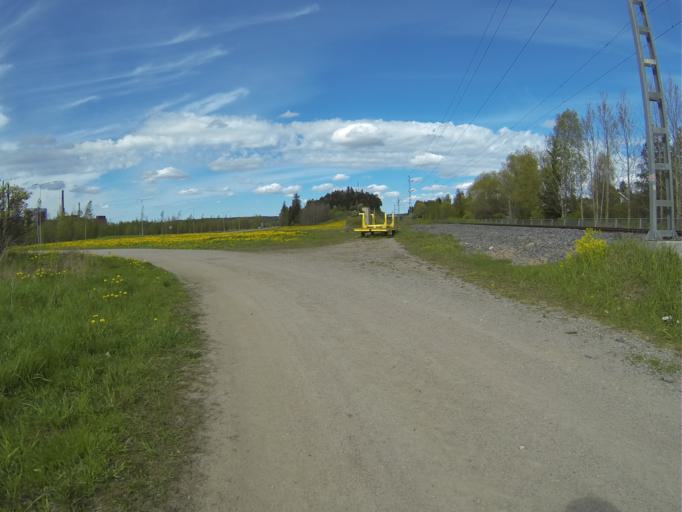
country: FI
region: Varsinais-Suomi
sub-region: Salo
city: Salo
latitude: 60.3676
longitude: 23.1189
